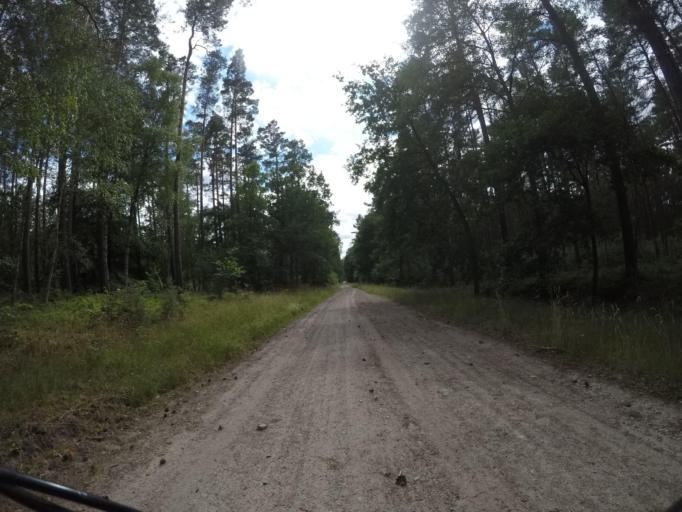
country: DE
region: Mecklenburg-Vorpommern
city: Lubtheen
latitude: 53.2693
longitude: 10.9893
